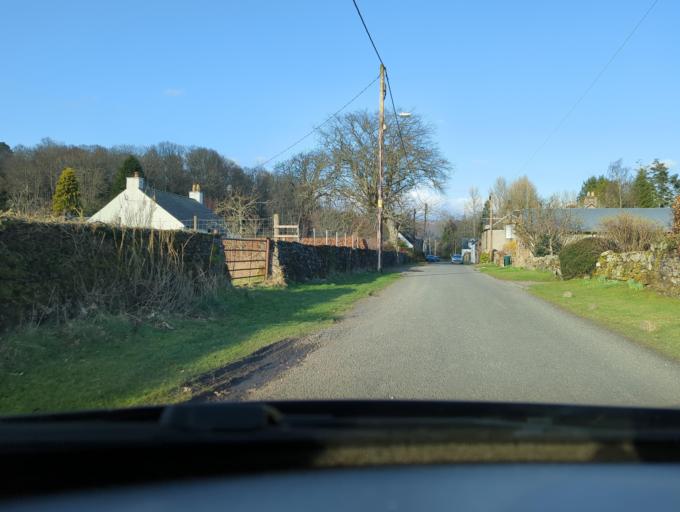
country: GB
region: Scotland
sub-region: Perth and Kinross
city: Comrie
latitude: 56.3719
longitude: -3.9991
